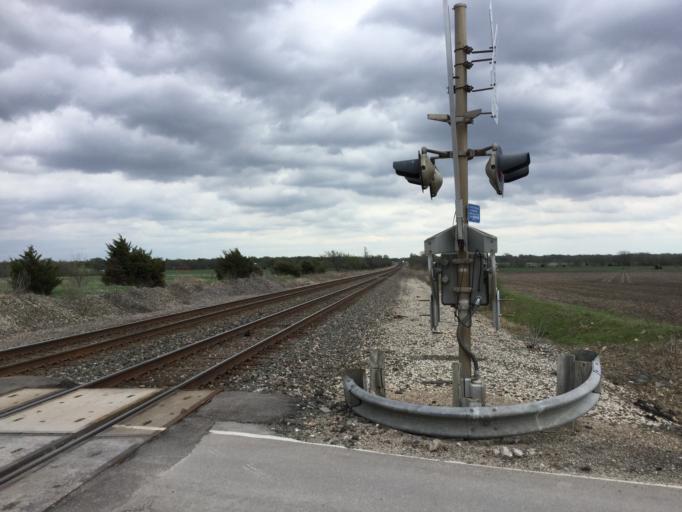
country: US
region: Kansas
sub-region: Osage County
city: Osage City
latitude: 38.4092
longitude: -95.8763
